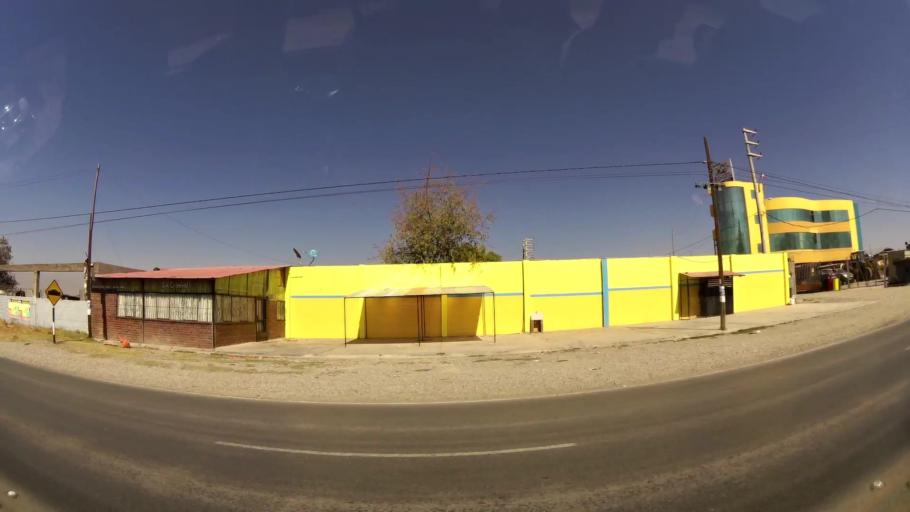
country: PE
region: Junin
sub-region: Provincia de Huancayo
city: San Agustin
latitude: -11.9870
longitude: -75.2598
